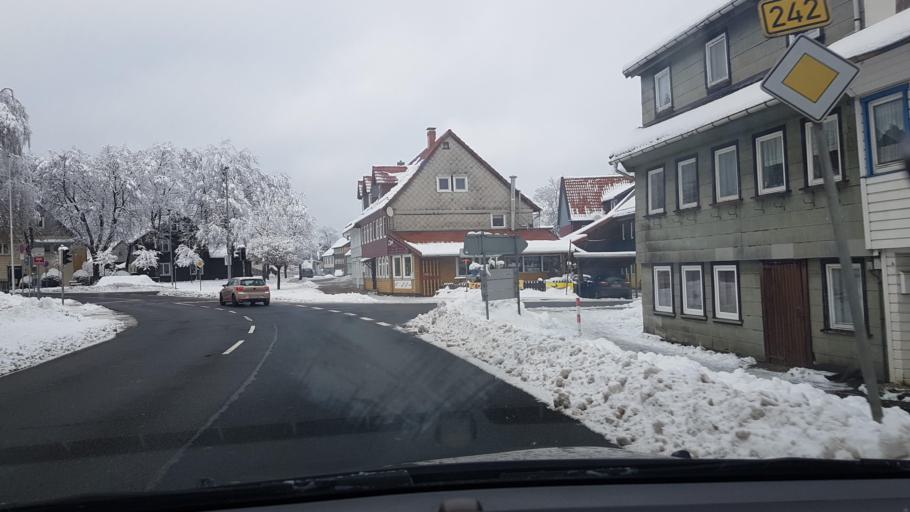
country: DE
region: Lower Saxony
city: Clausthal-Zellerfeld
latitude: 51.8012
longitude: 10.3389
